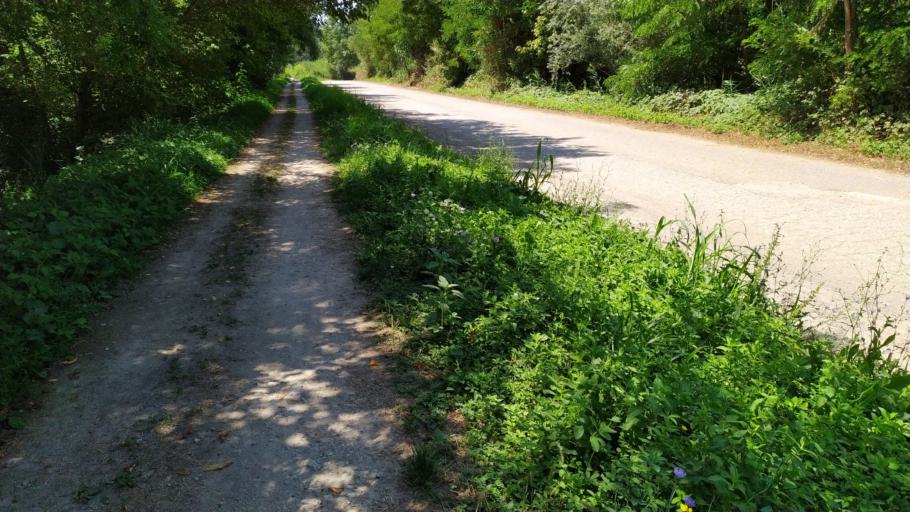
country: IT
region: Emilia-Romagna
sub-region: Forli-Cesena
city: Forli
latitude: 44.2060
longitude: 12.0101
